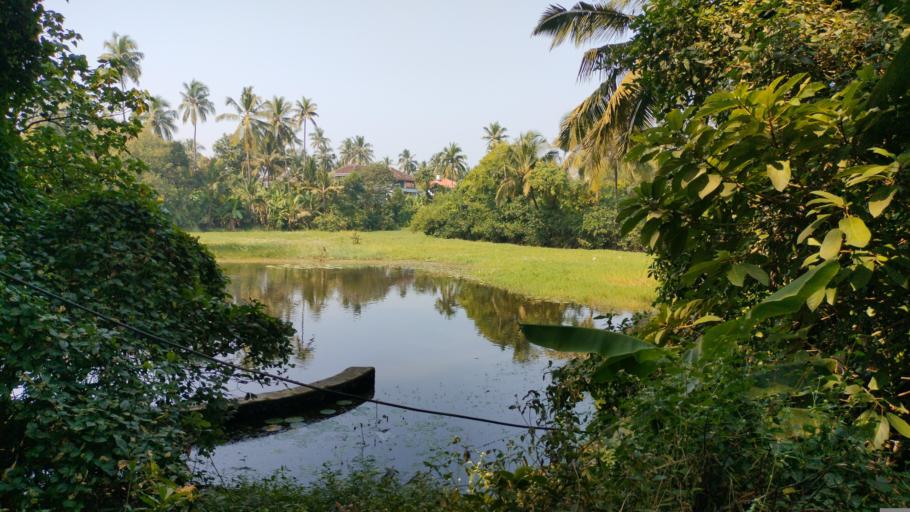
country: IN
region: Maharashtra
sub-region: Thane
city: Virar
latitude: 19.4366
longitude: 72.7817
